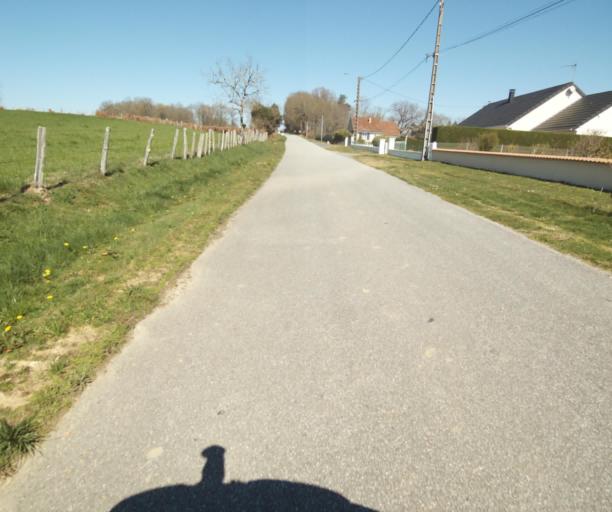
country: FR
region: Limousin
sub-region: Departement de la Correze
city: Saint-Mexant
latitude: 45.3113
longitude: 1.6473
